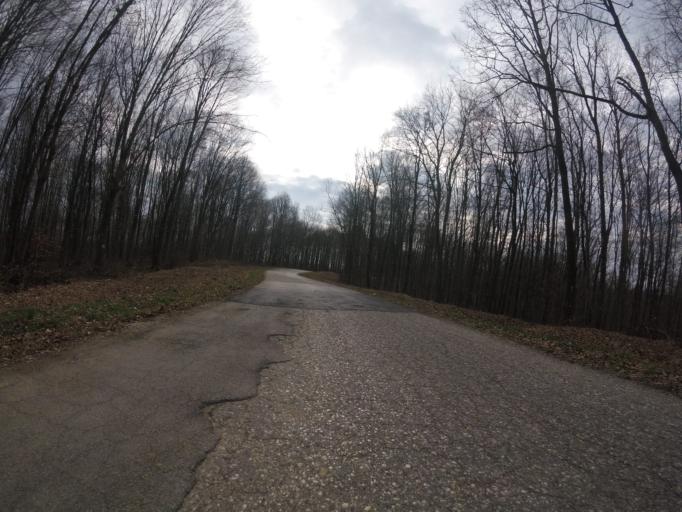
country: HR
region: Zagrebacka
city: Mraclin
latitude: 45.5221
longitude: 16.0482
